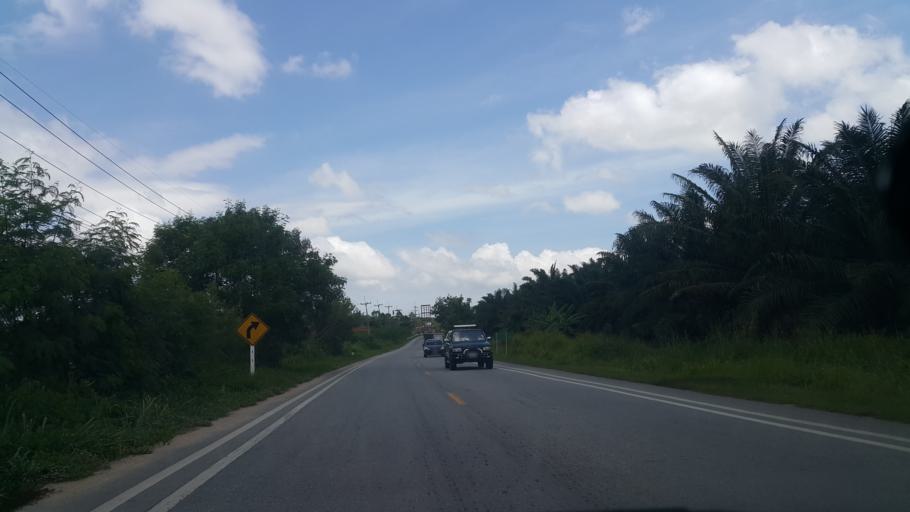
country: TH
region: Rayong
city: Ban Chang
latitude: 12.8142
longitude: 101.0595
